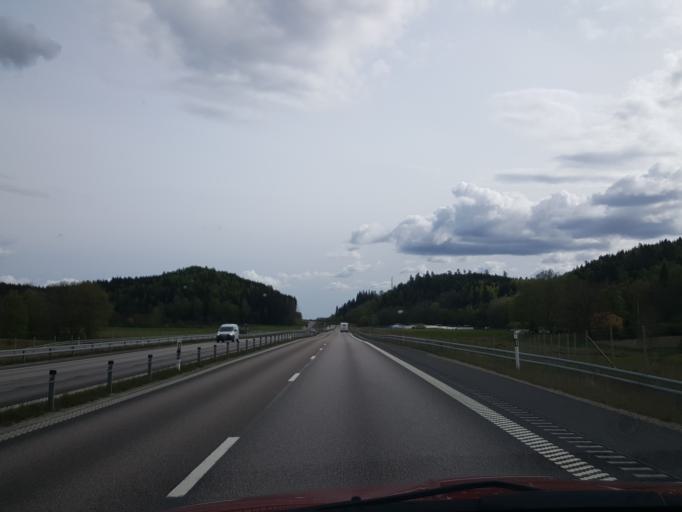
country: SE
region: Vaestra Goetaland
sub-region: Lilla Edets Kommun
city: Lilla Edet
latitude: 58.1911
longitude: 12.1458
